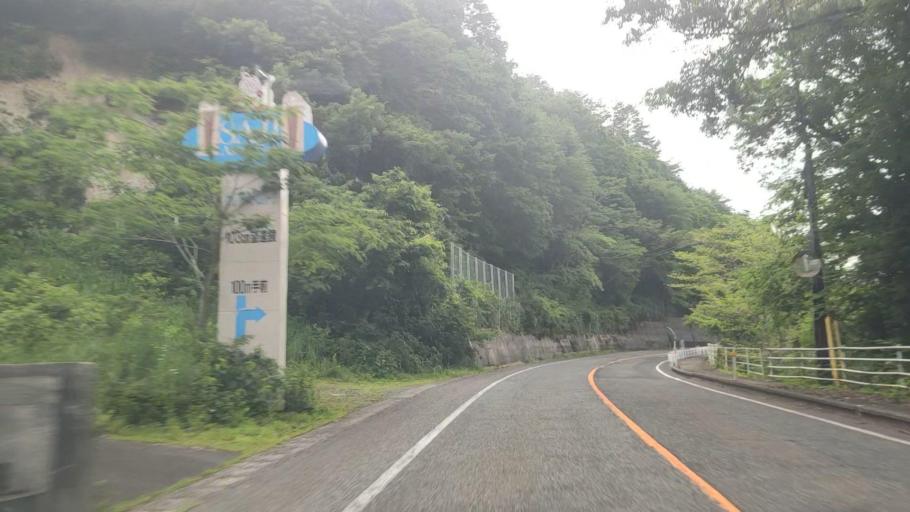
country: JP
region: Tottori
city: Kurayoshi
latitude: 35.2927
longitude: 133.9447
